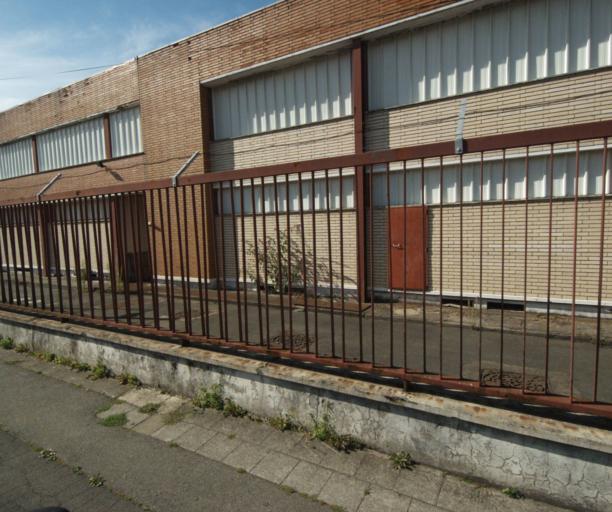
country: FR
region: Nord-Pas-de-Calais
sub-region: Departement du Nord
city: La Madeleine
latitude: 50.6369
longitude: 3.0952
